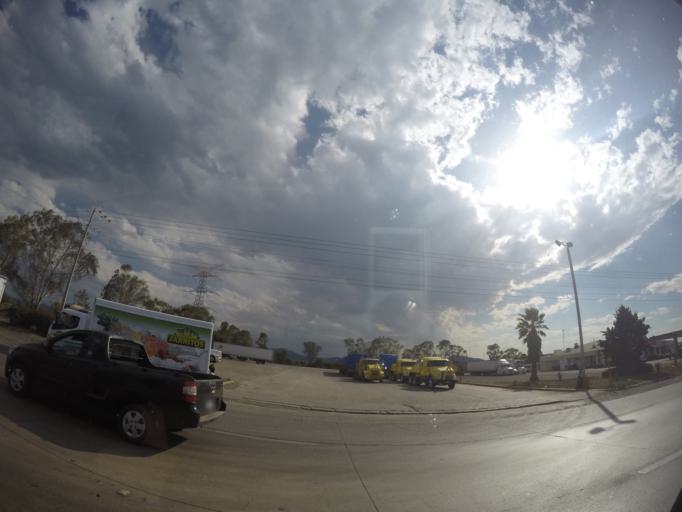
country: MX
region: Queretaro
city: El Sauz
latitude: 20.4820
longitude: -100.1142
